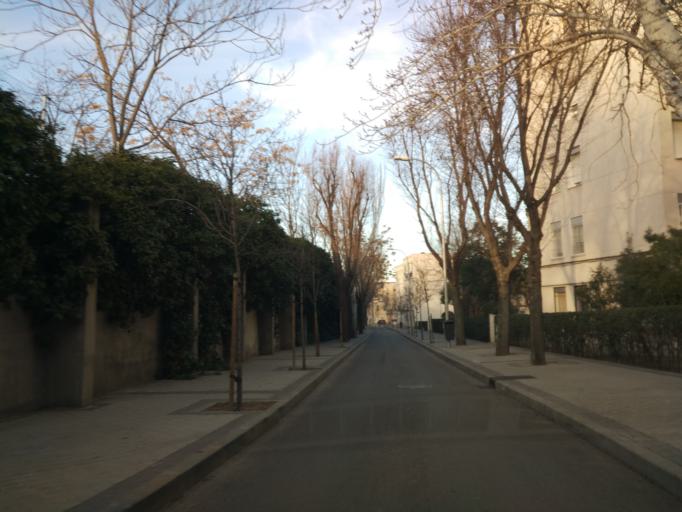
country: ES
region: Madrid
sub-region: Provincia de Madrid
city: Tetuan de las Victorias
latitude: 40.4600
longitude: -3.7149
